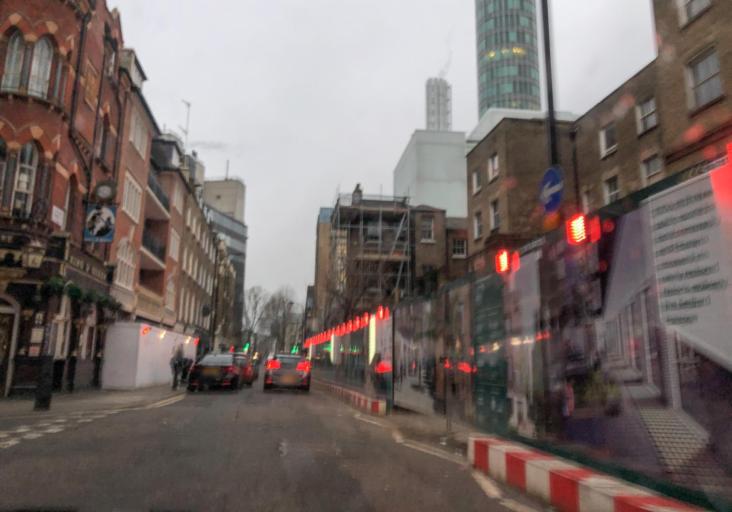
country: GB
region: England
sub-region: Greater London
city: London
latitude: 51.5201
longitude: -0.1382
